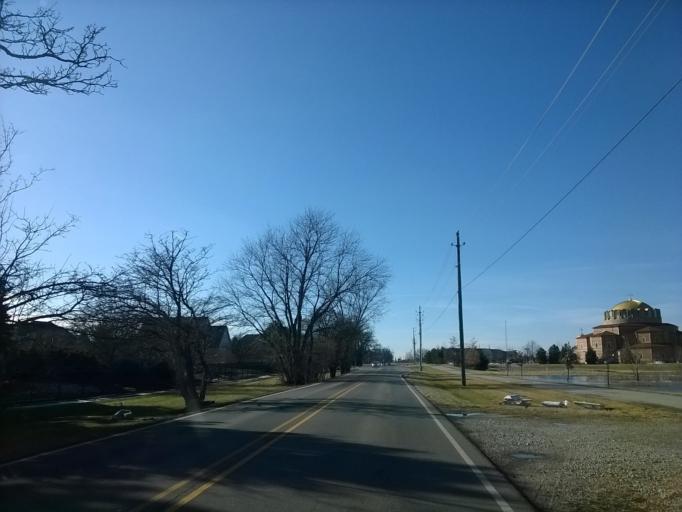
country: US
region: Indiana
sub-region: Boone County
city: Zionsville
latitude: 39.9411
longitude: -86.2181
